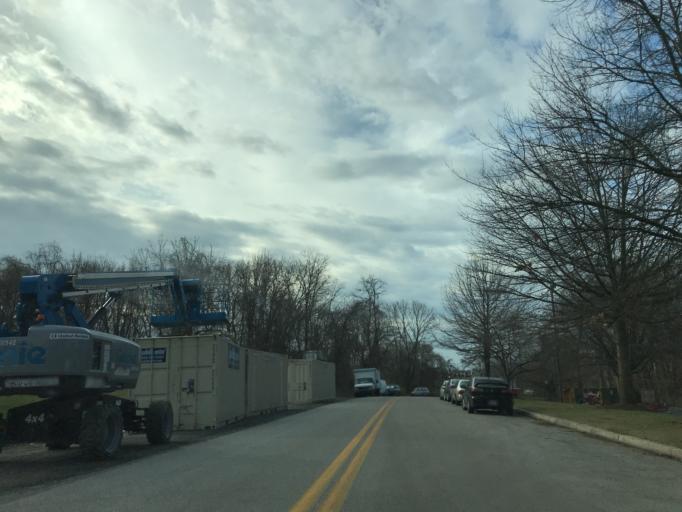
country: US
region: Maryland
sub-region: Anne Arundel County
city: Jessup
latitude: 39.1715
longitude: -76.7884
